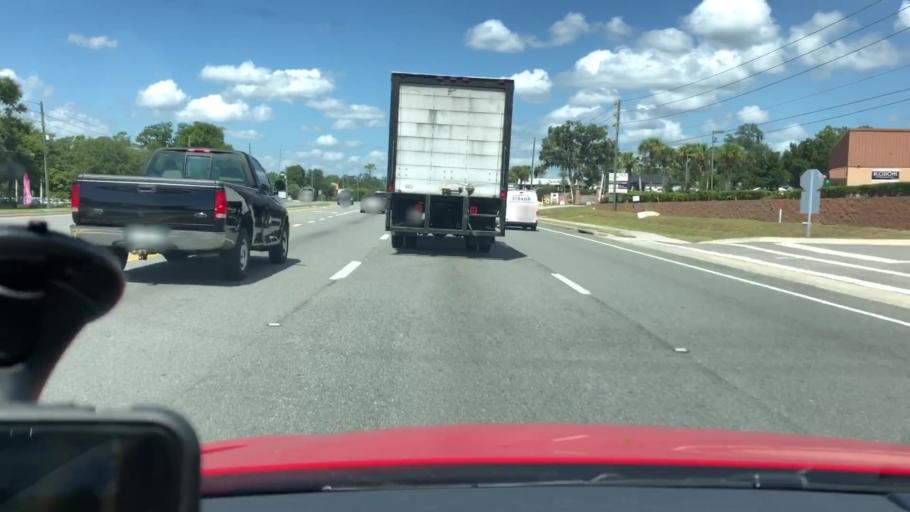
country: US
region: Florida
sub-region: Volusia County
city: De Land Southwest
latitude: 28.9883
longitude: -81.3003
